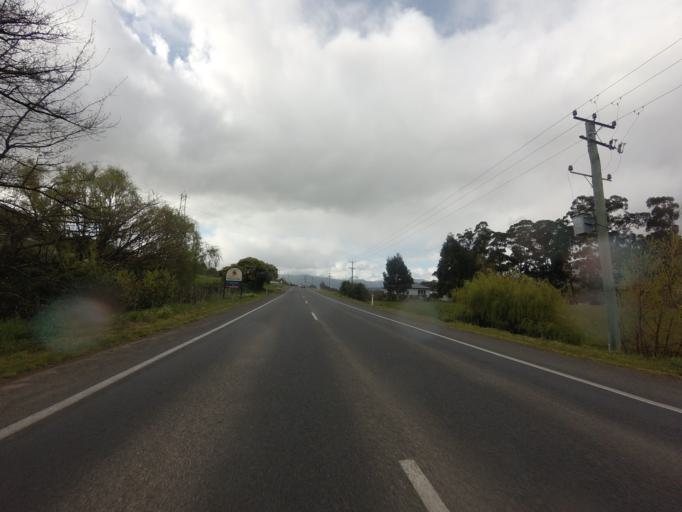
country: AU
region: Tasmania
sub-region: Huon Valley
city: Huonville
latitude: -43.0422
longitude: 147.0444
